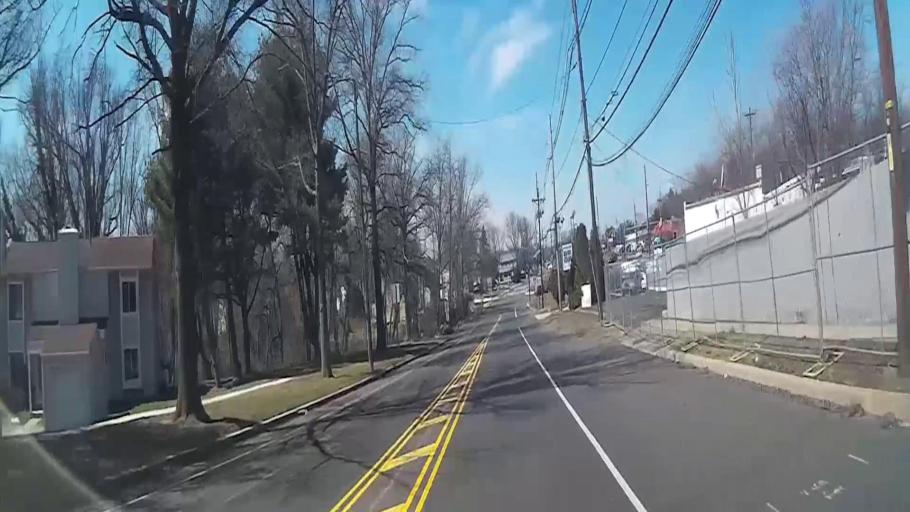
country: US
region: New Jersey
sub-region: Camden County
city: Greentree
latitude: 39.8951
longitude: -74.9441
